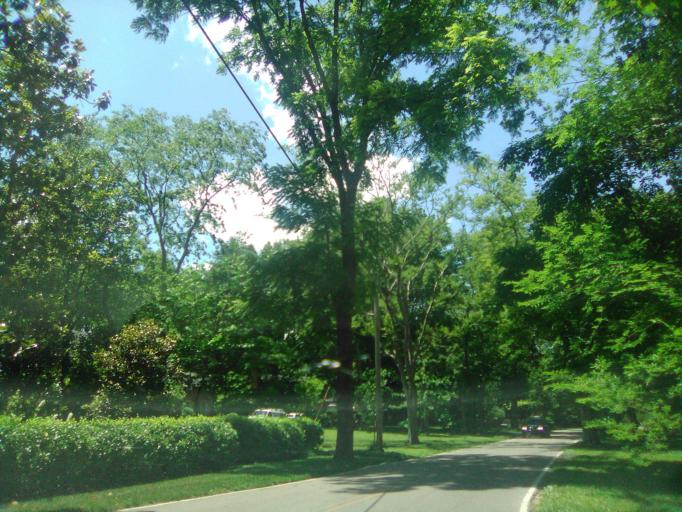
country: US
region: Tennessee
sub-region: Davidson County
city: Belle Meade
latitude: 36.1133
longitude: -86.8575
